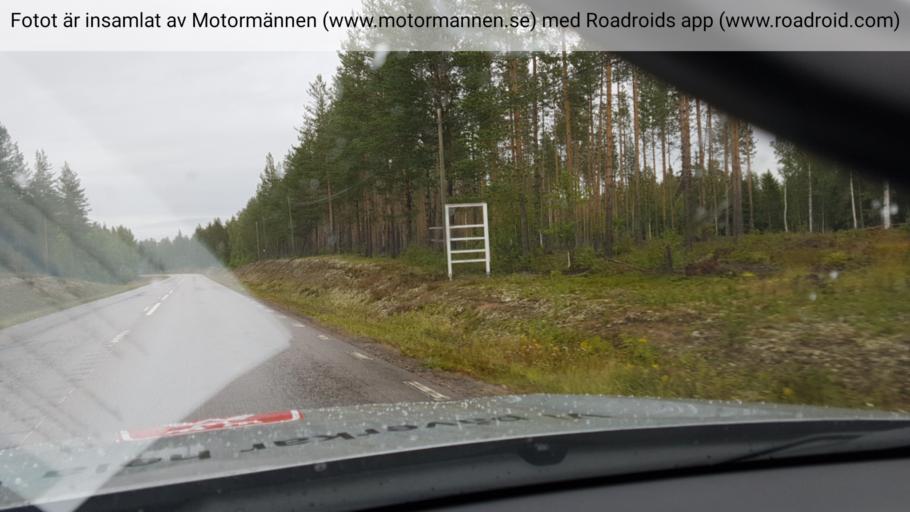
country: SE
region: Norrbotten
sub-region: Alvsbyns Kommun
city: AElvsbyn
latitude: 66.2240
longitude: 20.8752
